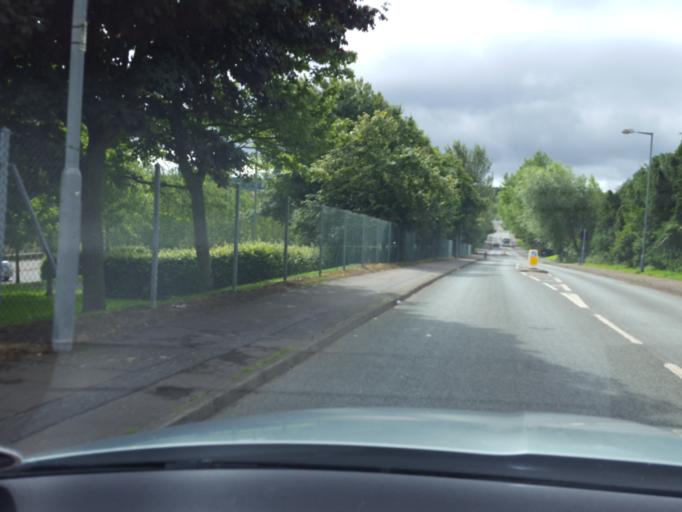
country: GB
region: Scotland
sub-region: Falkirk
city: Bo'ness
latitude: 56.0105
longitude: -3.5995
